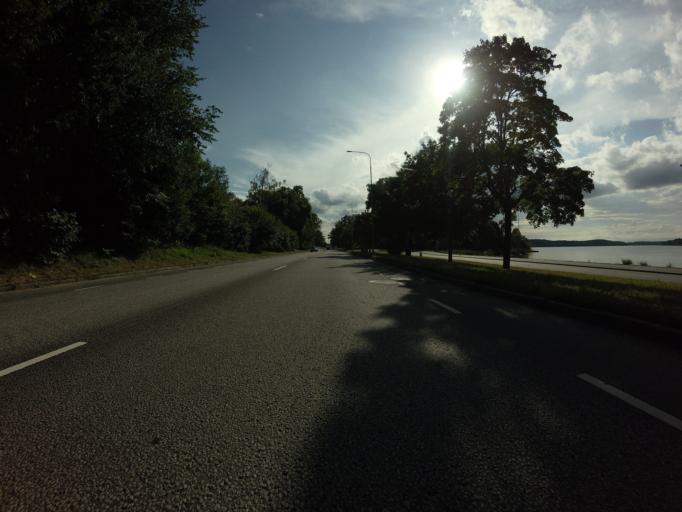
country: SE
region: Stockholm
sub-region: Lidingo
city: Lidingoe
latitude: 59.3683
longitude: 18.1192
